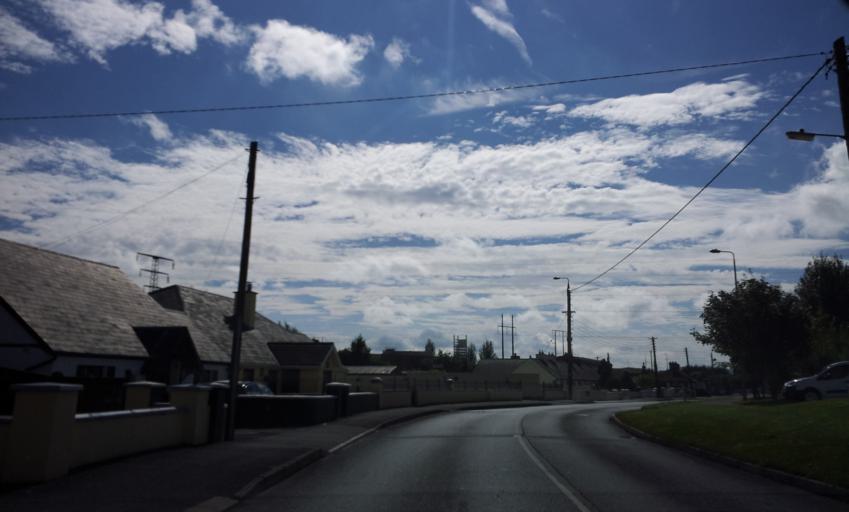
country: IE
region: Leinster
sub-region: Laois
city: Portlaoise
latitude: 53.0302
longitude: -7.2918
